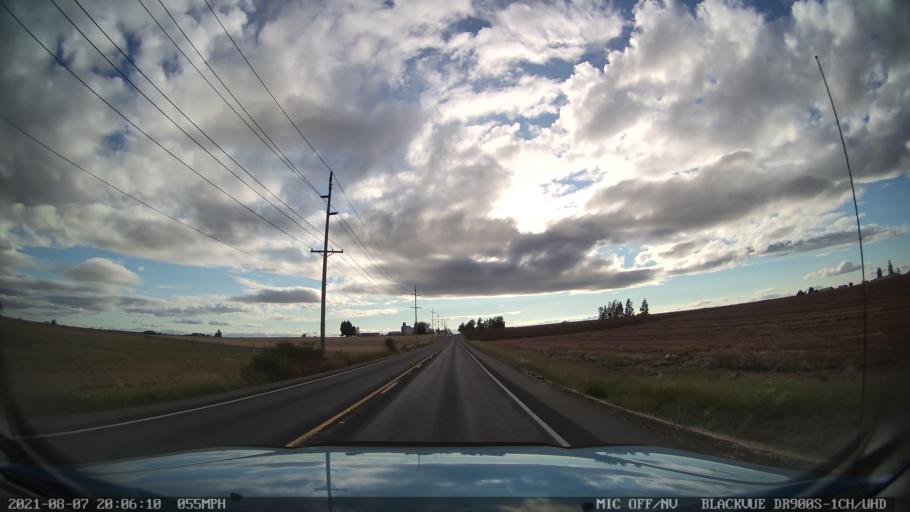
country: US
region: Oregon
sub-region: Marion County
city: Silverton
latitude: 44.9914
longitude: -122.8634
